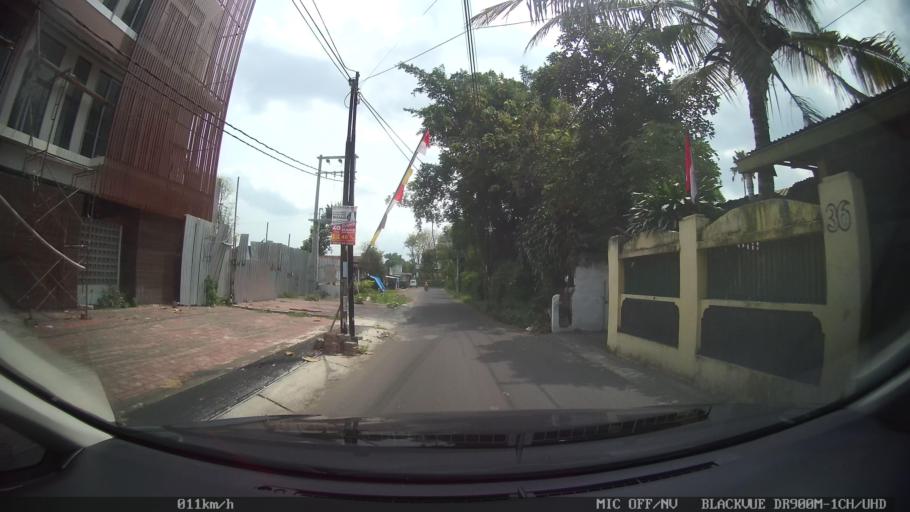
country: ID
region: Daerah Istimewa Yogyakarta
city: Depok
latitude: -7.7849
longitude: 110.4052
